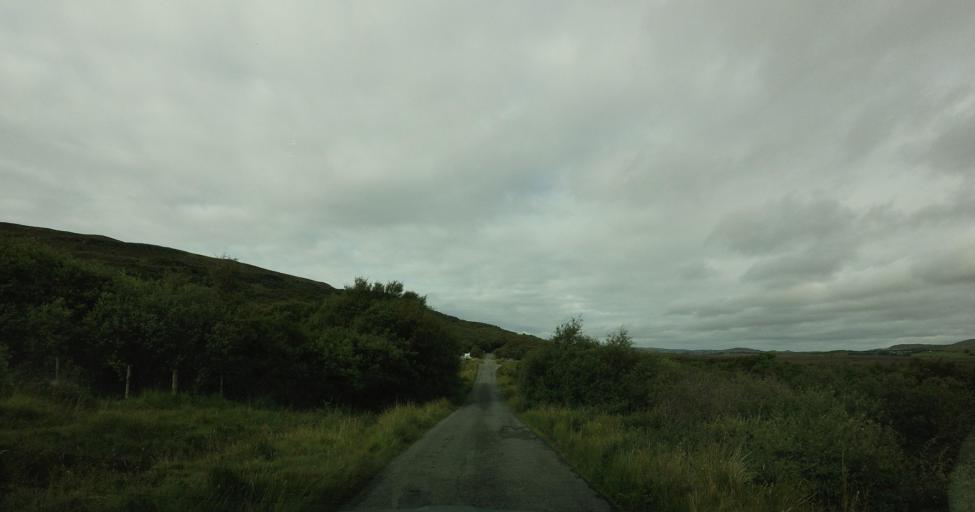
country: GB
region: Scotland
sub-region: Highland
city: Portree
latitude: 57.4174
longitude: -6.2317
